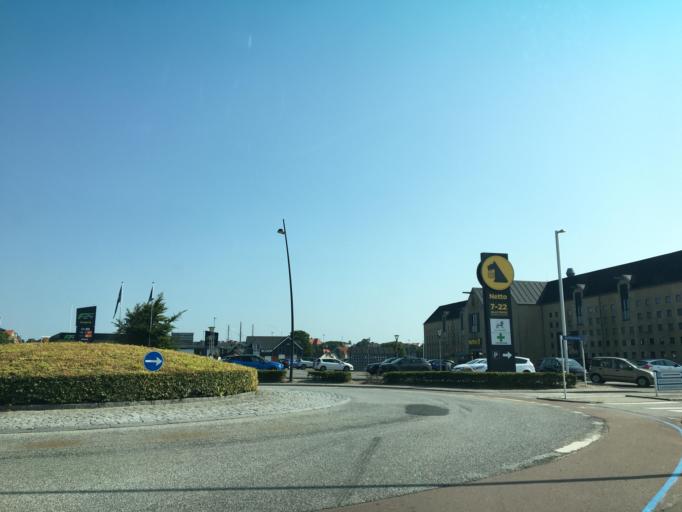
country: DK
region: North Denmark
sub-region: Thisted Kommune
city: Thisted
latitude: 56.9516
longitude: 8.6918
